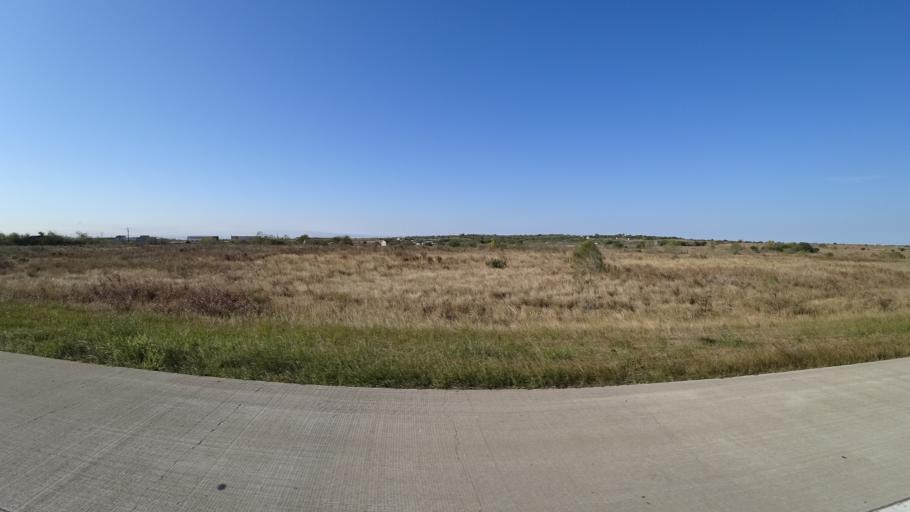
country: US
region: Texas
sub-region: Travis County
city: Onion Creek
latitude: 30.1269
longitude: -97.6633
